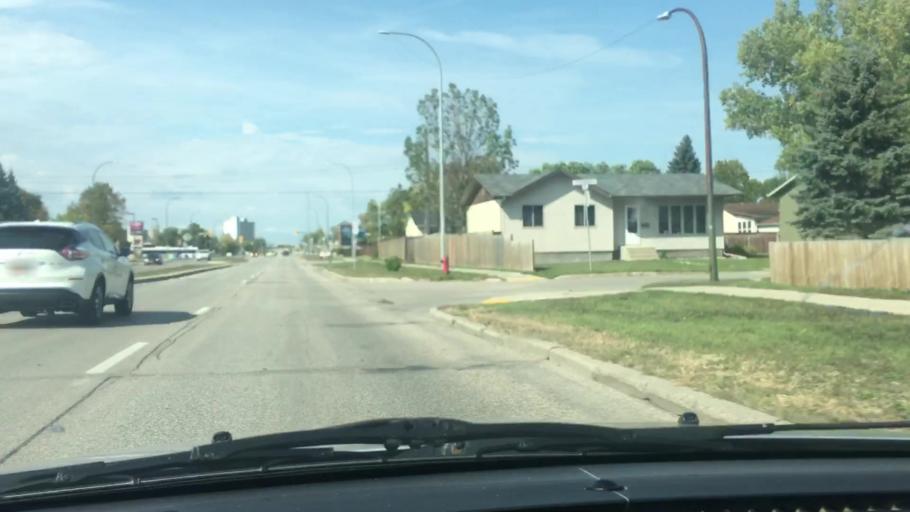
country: CA
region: Manitoba
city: Winnipeg
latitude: 49.8255
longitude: -97.1028
